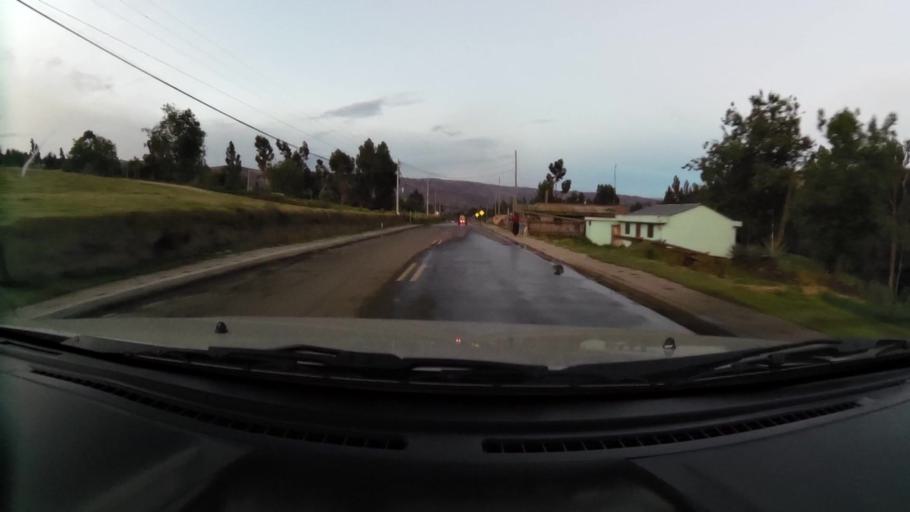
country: EC
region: Chimborazo
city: Riobamba
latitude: -1.9124
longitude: -78.6977
